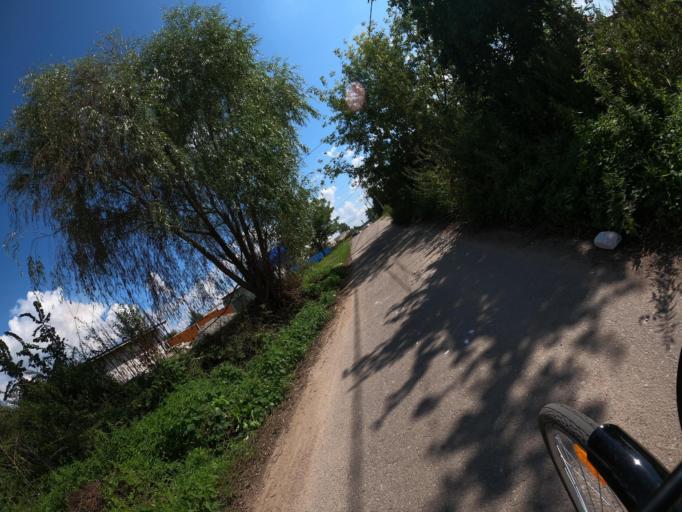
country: RU
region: Moskovskaya
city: Voskresensk
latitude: 55.2962
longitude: 38.6700
